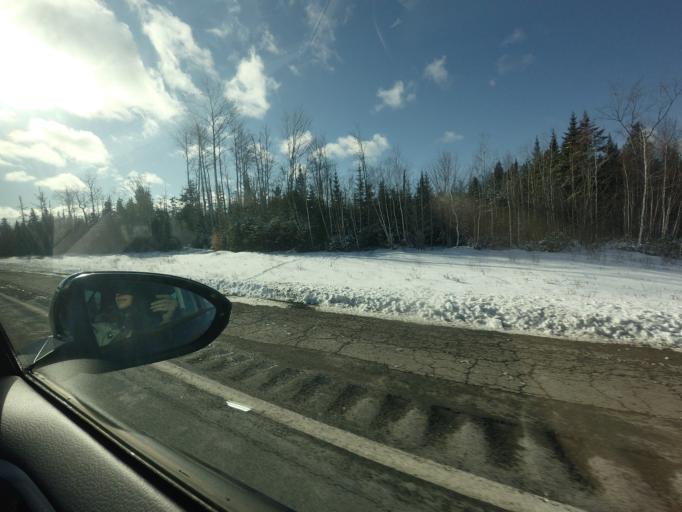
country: CA
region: New Brunswick
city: Fredericton
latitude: 45.8858
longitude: -66.6409
